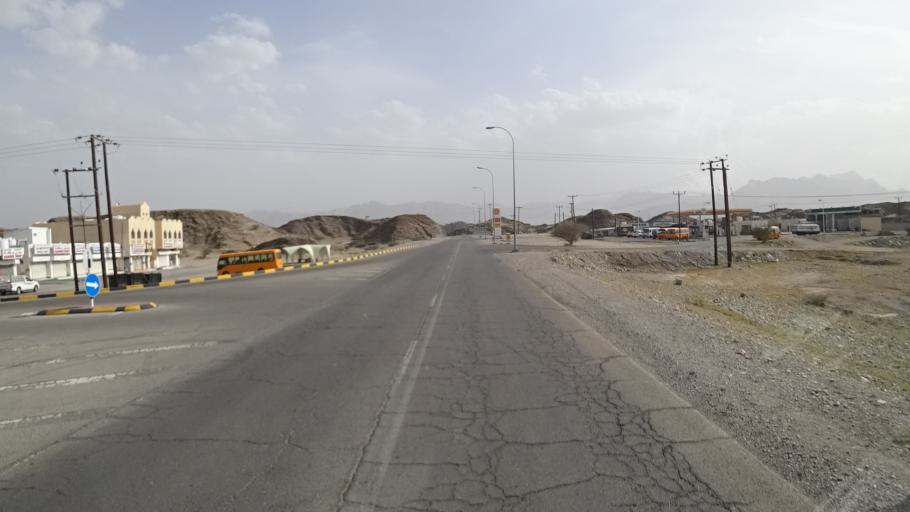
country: OM
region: Muhafazat Masqat
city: Bawshar
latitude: 23.3848
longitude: 58.5129
